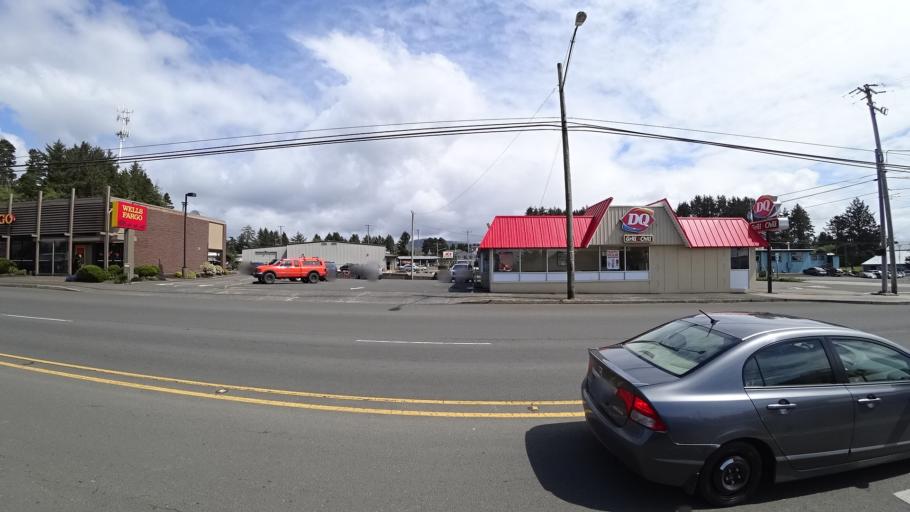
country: US
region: Oregon
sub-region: Lincoln County
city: Lincoln City
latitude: 44.9819
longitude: -124.0076
